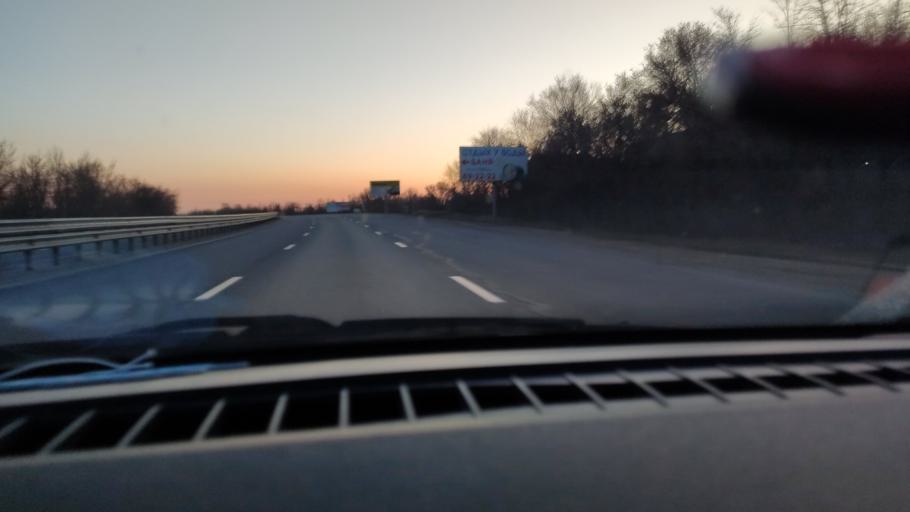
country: RU
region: Saratov
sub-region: Saratovskiy Rayon
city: Saratov
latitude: 51.6511
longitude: 45.9962
